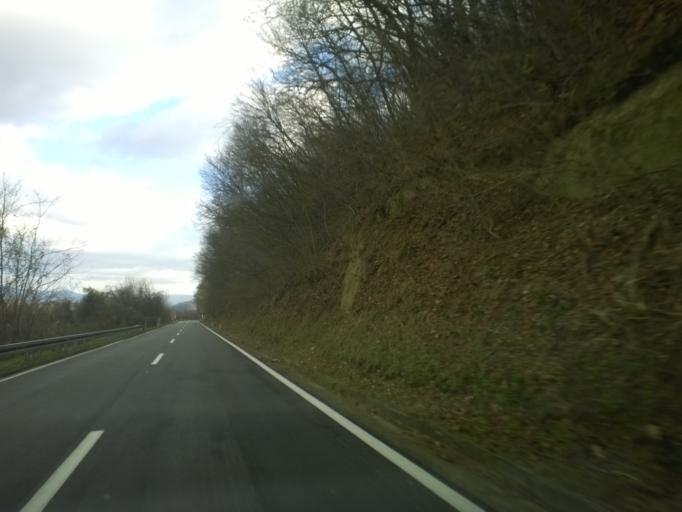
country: RO
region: Caras-Severin
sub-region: Comuna Berzasca
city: Liubcova
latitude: 44.6445
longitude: 21.8771
